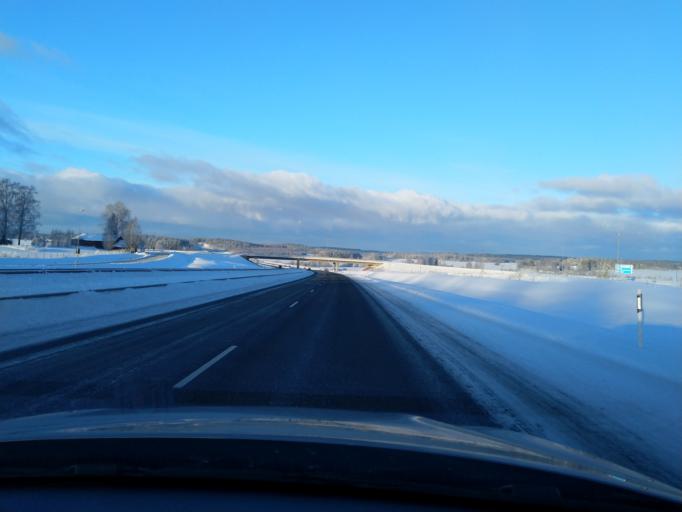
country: FI
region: Varsinais-Suomi
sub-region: Salo
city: Suomusjaervi
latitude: 60.3881
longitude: 23.5902
